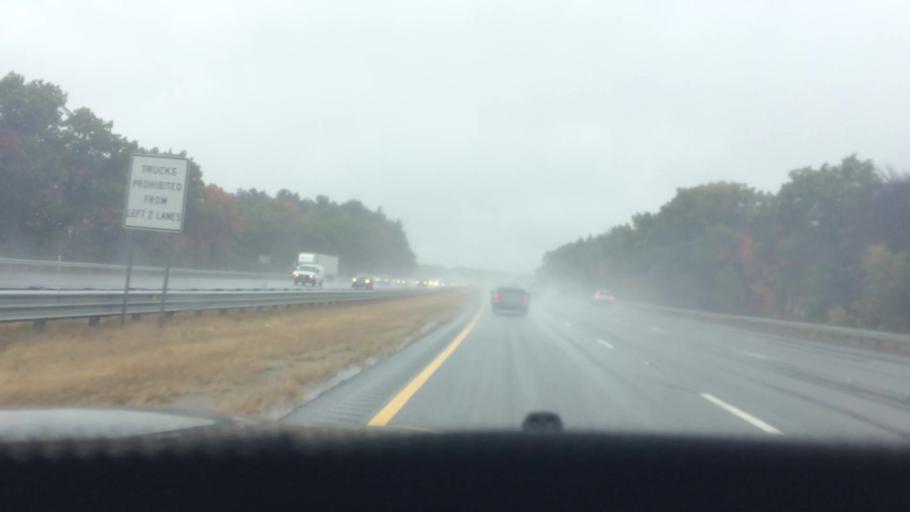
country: US
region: Massachusetts
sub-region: Middlesex County
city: Wilmington
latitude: 42.5443
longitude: -71.1353
